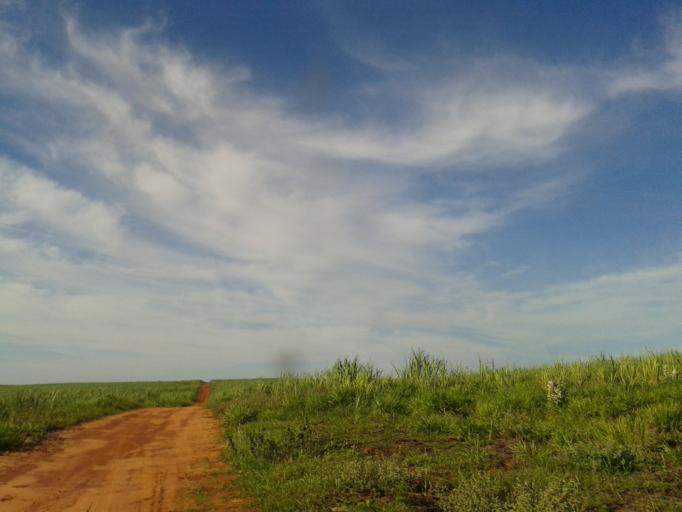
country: BR
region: Minas Gerais
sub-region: Santa Vitoria
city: Santa Vitoria
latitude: -19.1219
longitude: -50.0028
